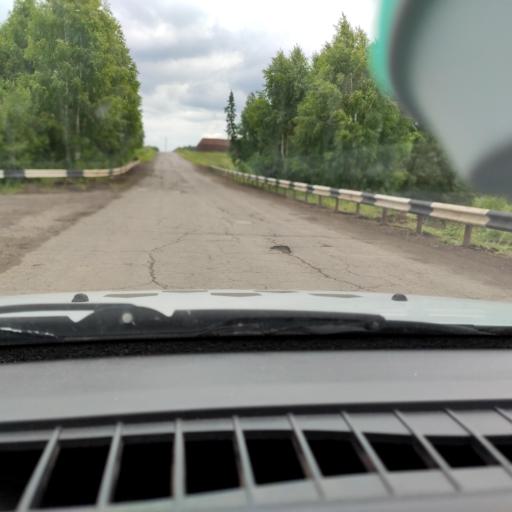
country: RU
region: Perm
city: Uinskoye
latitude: 57.1387
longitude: 56.5672
